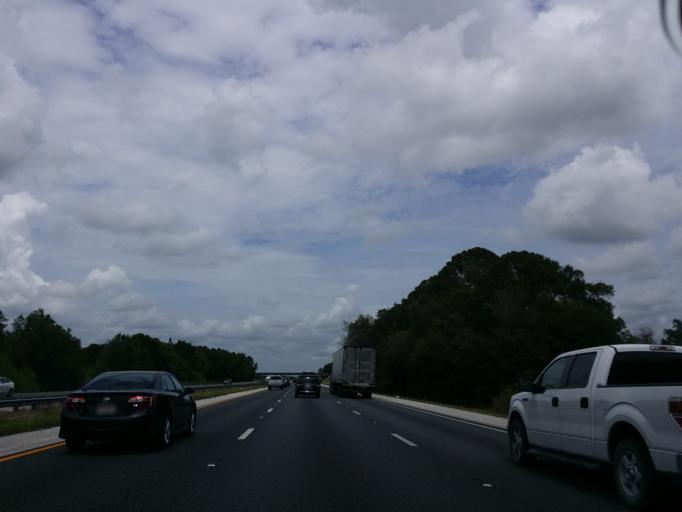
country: US
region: Florida
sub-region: Sumter County
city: Wildwood
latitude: 28.9255
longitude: -82.1120
